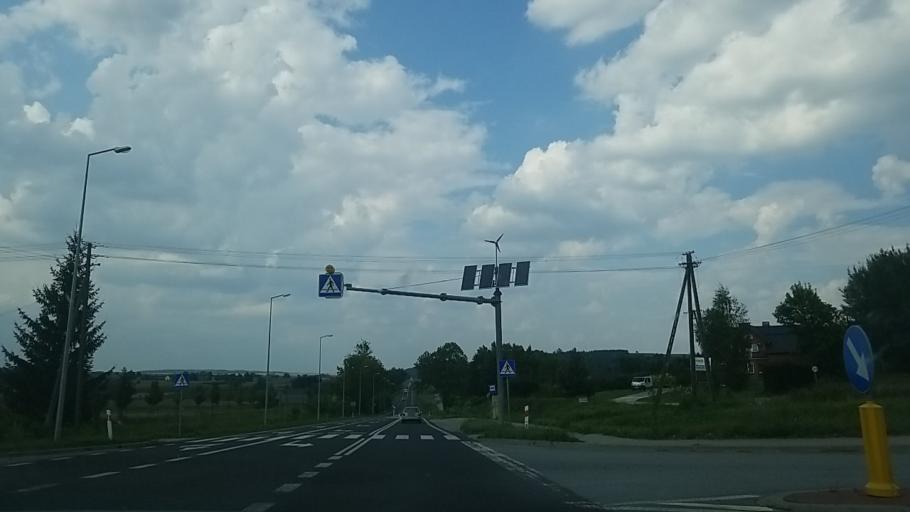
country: PL
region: Lublin Voivodeship
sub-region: Powiat bilgorajski
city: Goraj
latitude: 50.7308
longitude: 22.6673
